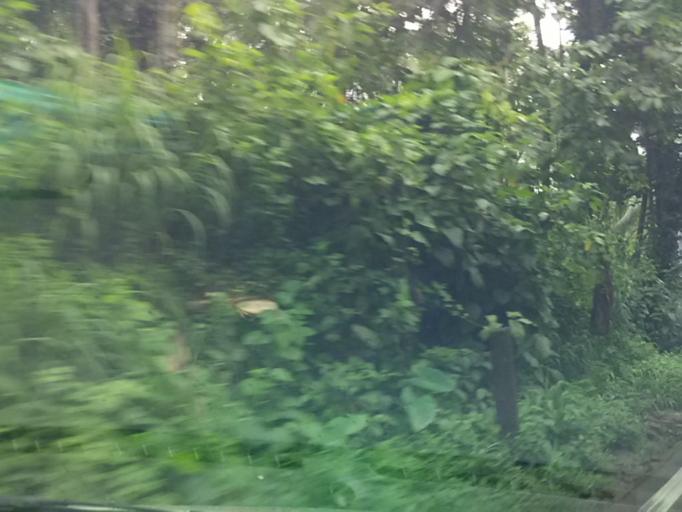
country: IN
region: Kerala
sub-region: Kozhikode
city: Kunnamangalam
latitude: 11.3113
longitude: 75.9142
